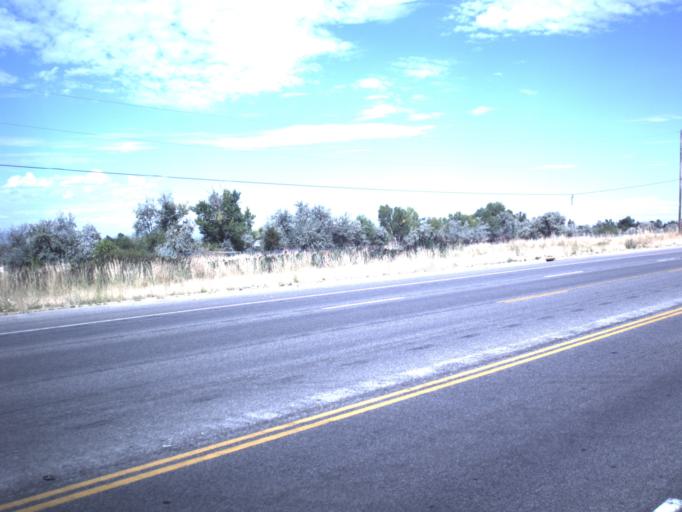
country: US
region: Utah
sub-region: Weber County
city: Harrisville
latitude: 41.2868
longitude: -111.9893
